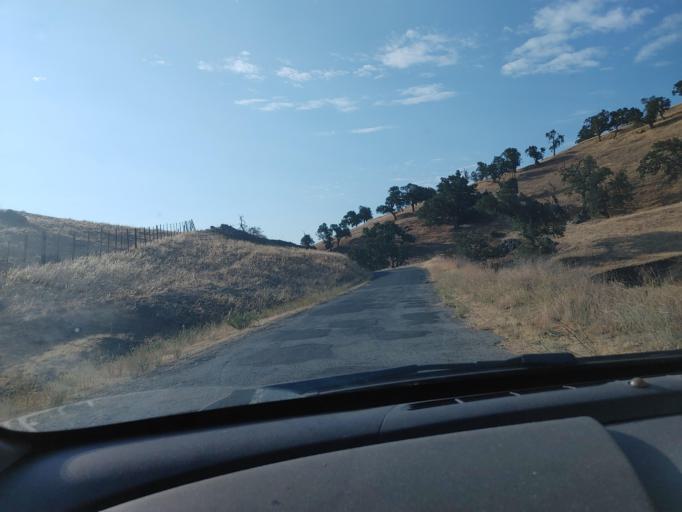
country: US
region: California
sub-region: San Benito County
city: Ridgemark
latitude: 36.7545
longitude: -121.1645
